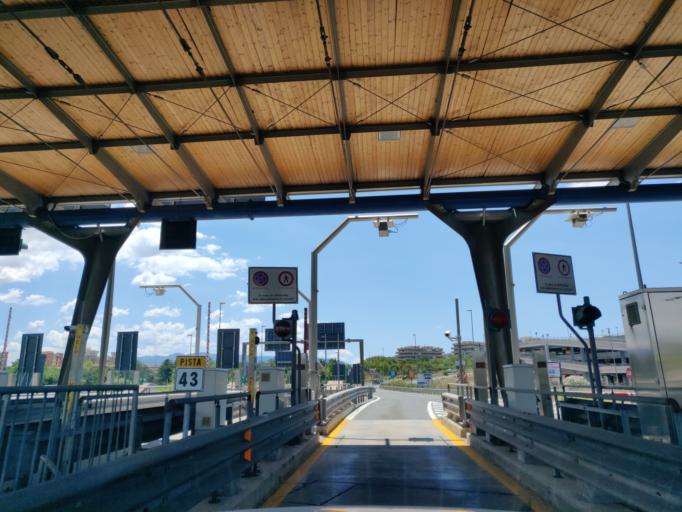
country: IT
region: Latium
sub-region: Citta metropolitana di Roma Capitale
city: Setteville
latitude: 41.9150
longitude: 12.6640
